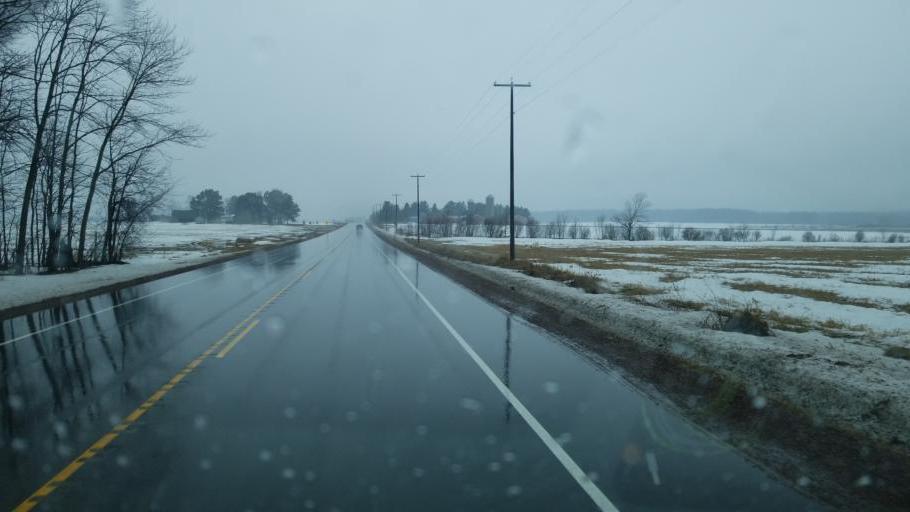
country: US
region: Wisconsin
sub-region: Marathon County
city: Spencer
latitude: 44.6563
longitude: -90.2924
